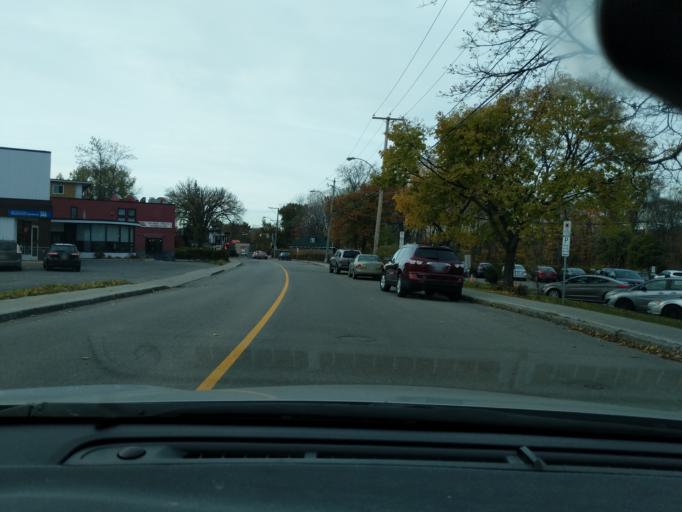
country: CA
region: Quebec
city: Quebec
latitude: 46.7843
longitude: -71.2460
